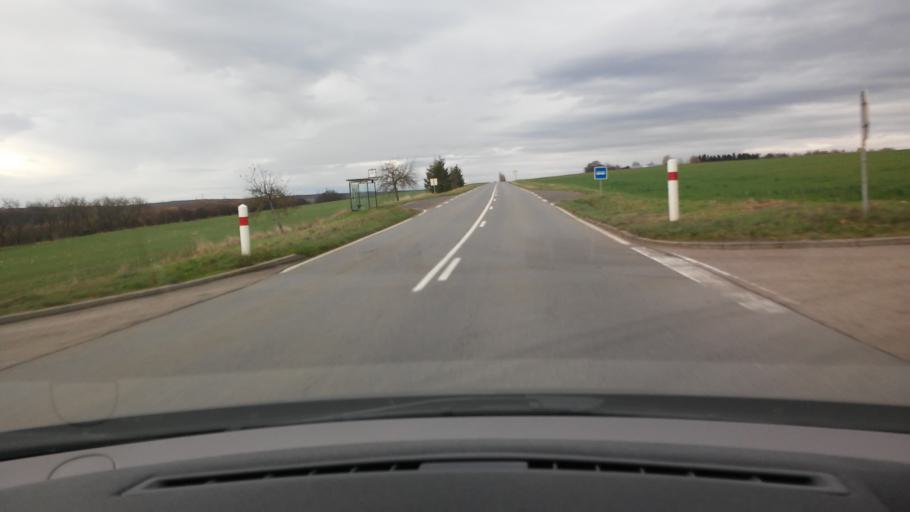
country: FR
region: Lorraine
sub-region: Departement de la Moselle
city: Retonfey
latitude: 49.1622
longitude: 6.2903
